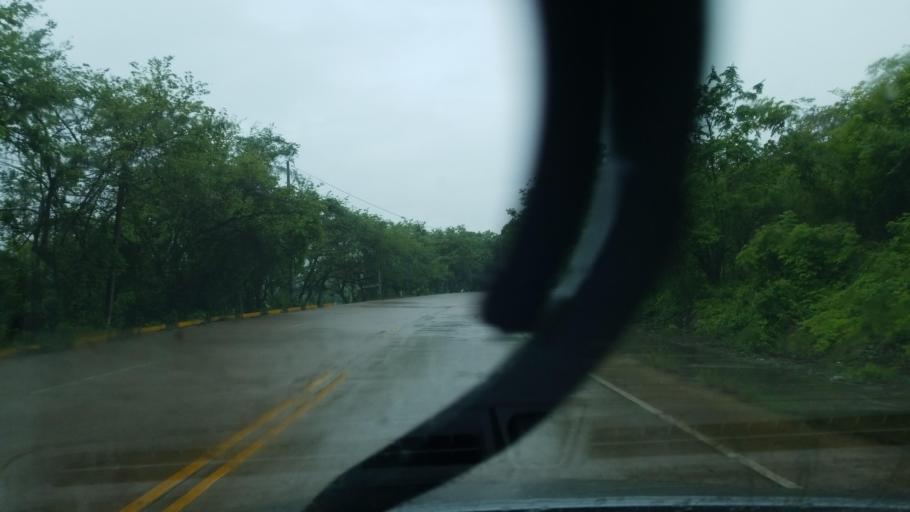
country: HN
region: Copan
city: Copan
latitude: 14.8463
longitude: -89.1353
